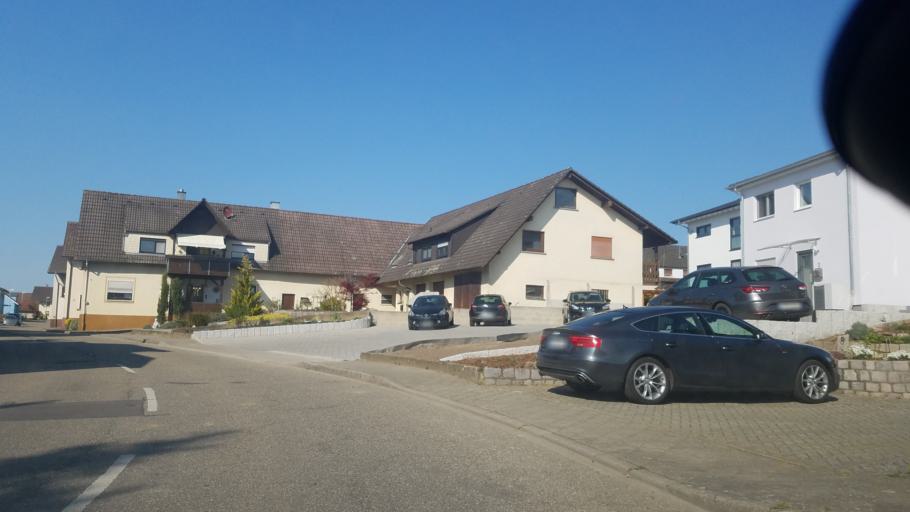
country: DE
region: Baden-Wuerttemberg
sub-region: Karlsruhe Region
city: Ottenhofen
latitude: 48.7479
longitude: 8.0948
